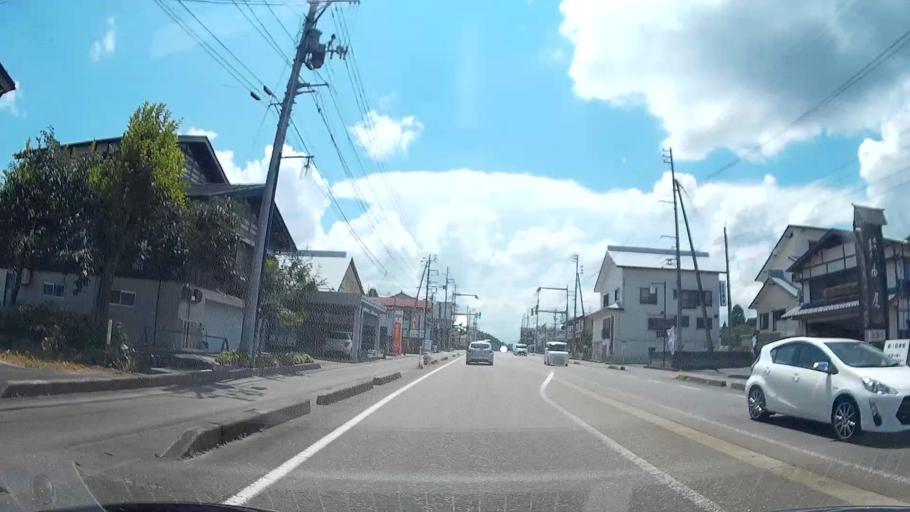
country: JP
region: Niigata
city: Tokamachi
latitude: 37.0986
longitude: 138.7335
